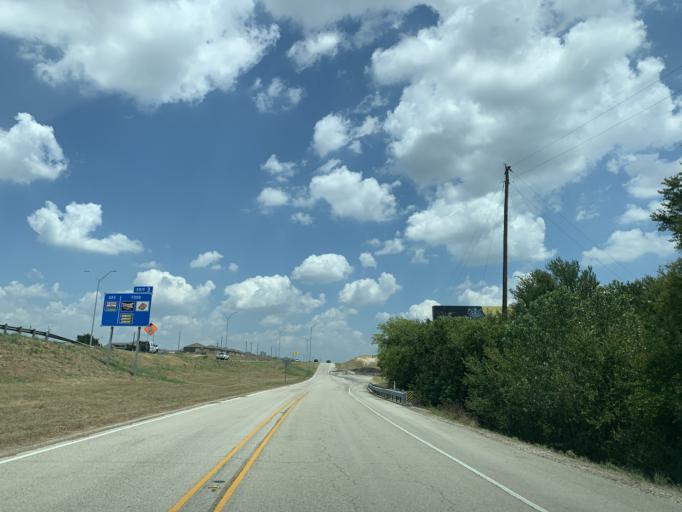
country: US
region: Texas
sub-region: Tarrant County
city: White Settlement
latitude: 32.7231
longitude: -97.5164
